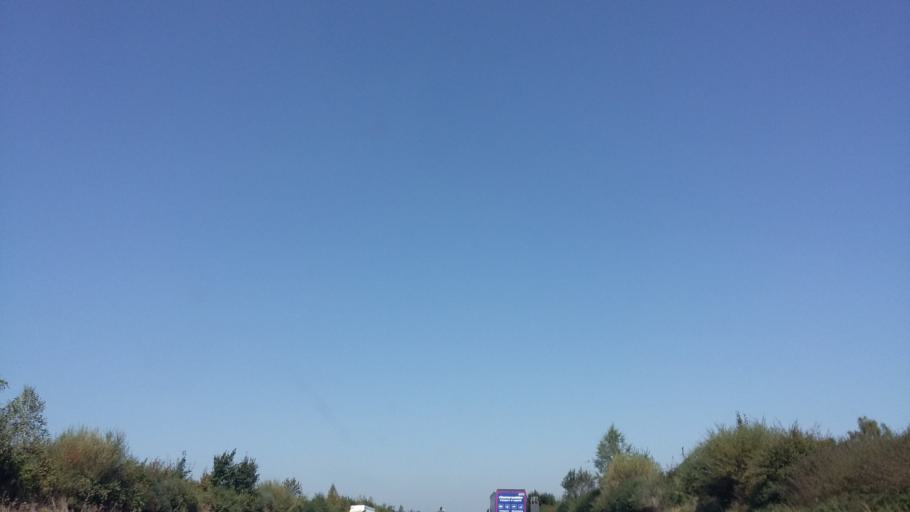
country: DE
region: Bavaria
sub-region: Upper Bavaria
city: Hurlach
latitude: 48.1354
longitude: 10.8324
